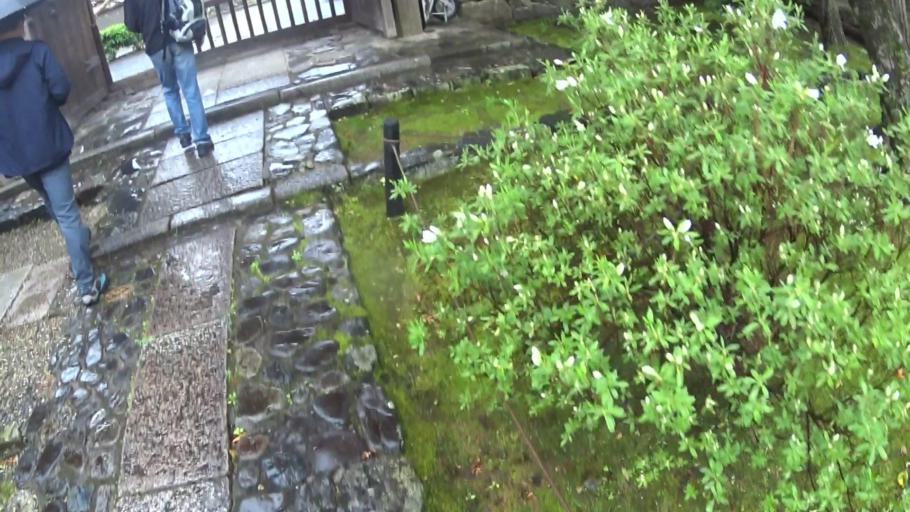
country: JP
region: Kyoto
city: Muko
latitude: 35.0155
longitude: 135.6847
